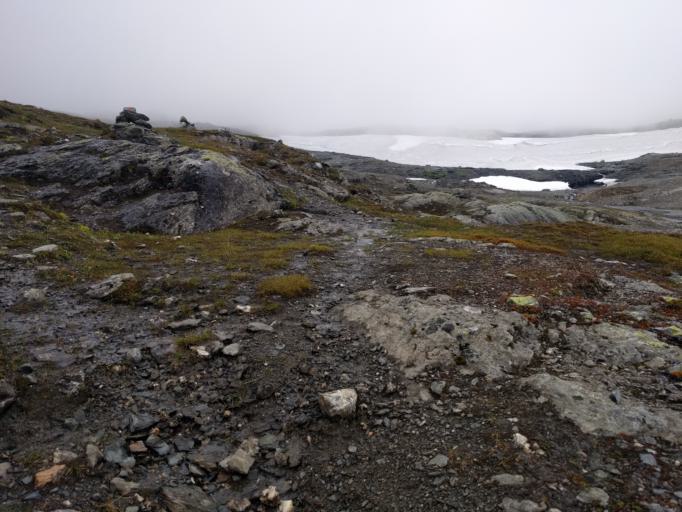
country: NO
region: Hordaland
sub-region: Eidfjord
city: Eidfjord
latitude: 60.0021
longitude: 7.1365
